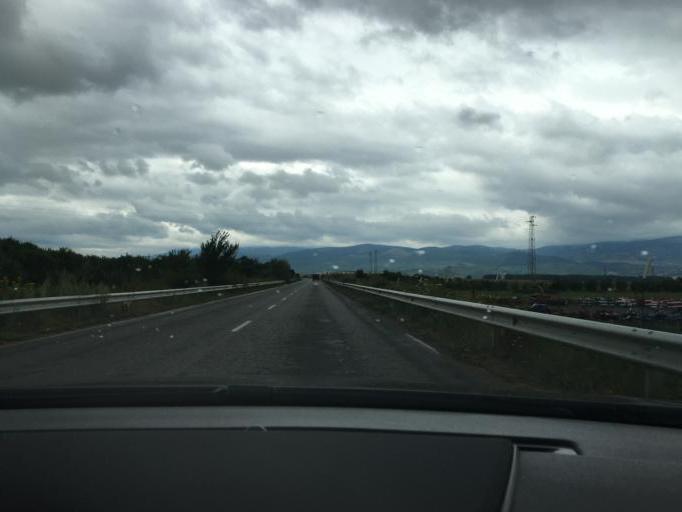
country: BG
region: Kyustendil
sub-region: Obshtina Kyustendil
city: Kyustendil
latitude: 42.2846
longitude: 22.7202
